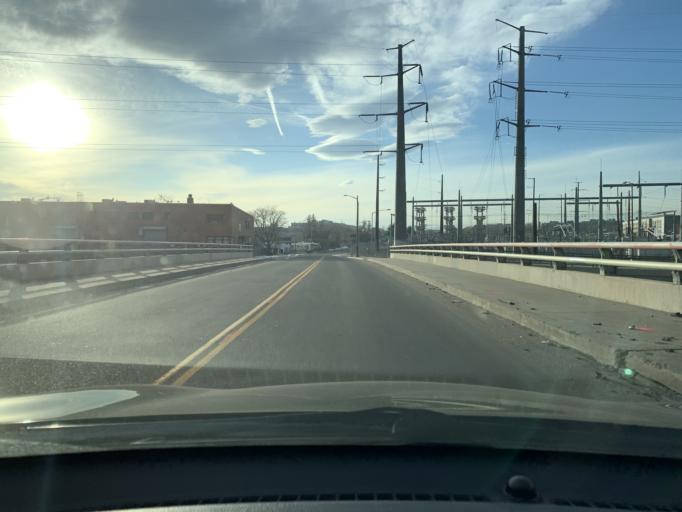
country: US
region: Colorado
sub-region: Denver County
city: Denver
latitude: 39.7369
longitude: -105.0172
